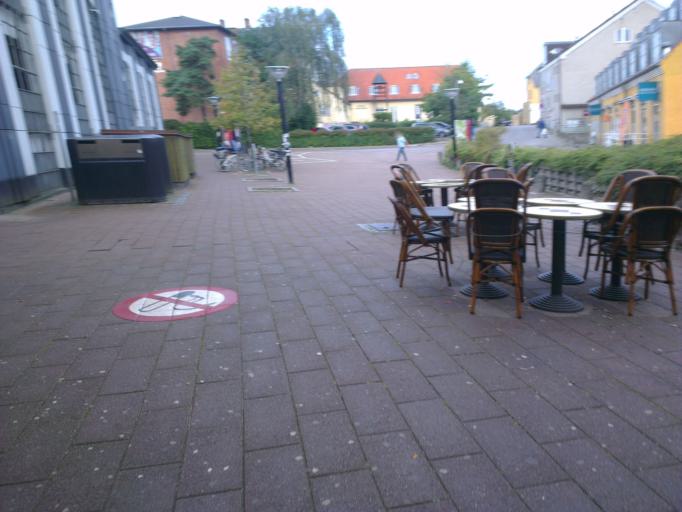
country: DK
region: Capital Region
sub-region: Hillerod Kommune
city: Hillerod
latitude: 55.9298
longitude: 12.2991
